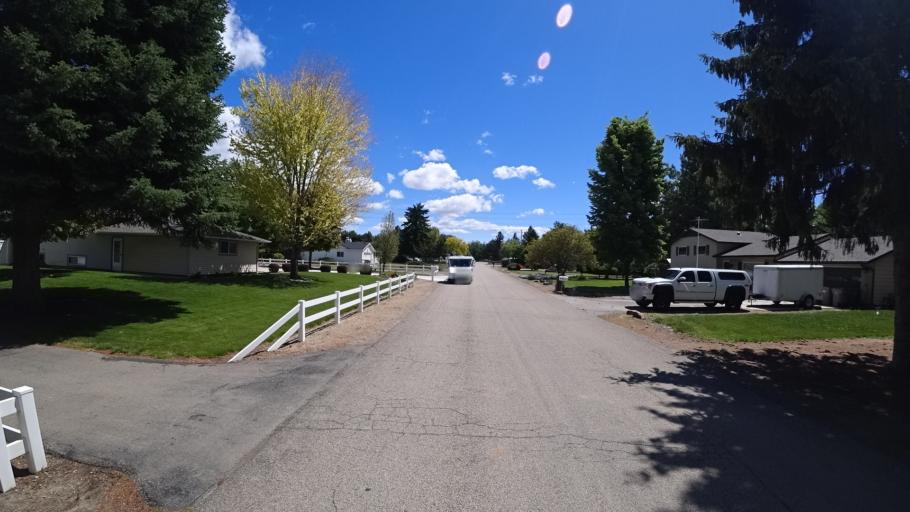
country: US
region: Idaho
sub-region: Ada County
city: Meridian
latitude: 43.6249
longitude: -116.3362
